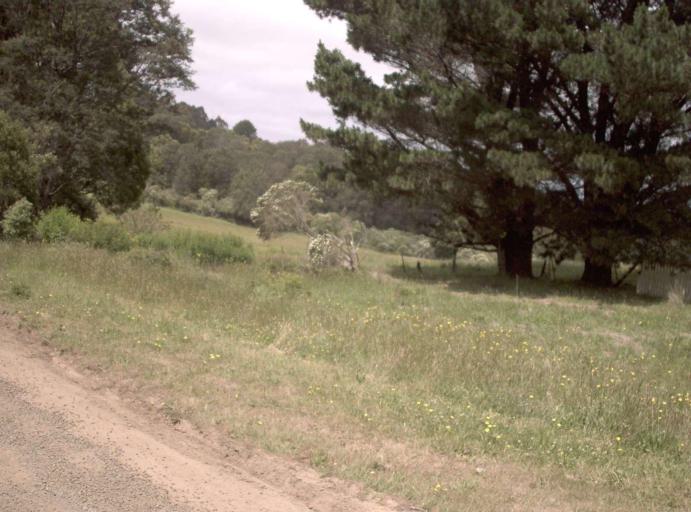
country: AU
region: Victoria
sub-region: Latrobe
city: Traralgon
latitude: -38.4152
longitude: 146.6172
